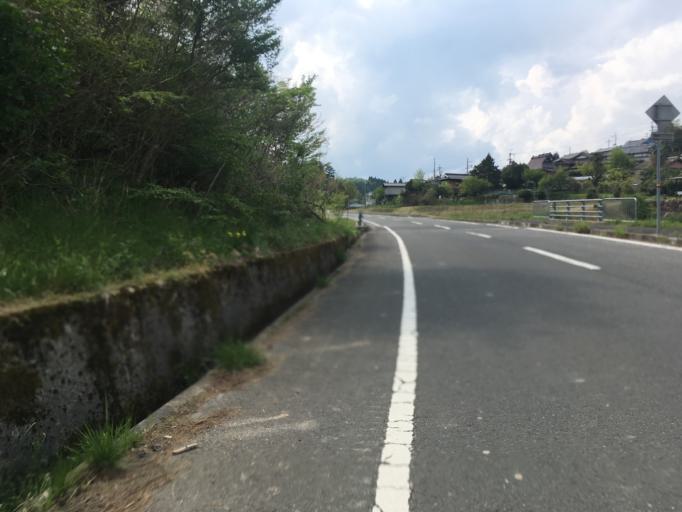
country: JP
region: Kyoto
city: Kameoka
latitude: 35.1084
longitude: 135.5799
